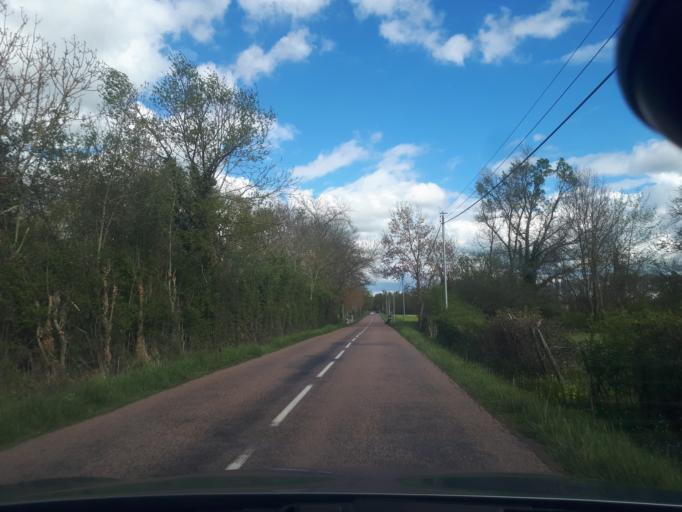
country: FR
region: Rhone-Alpes
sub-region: Departement de la Loire
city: Balbigny
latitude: 45.8149
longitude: 4.2075
